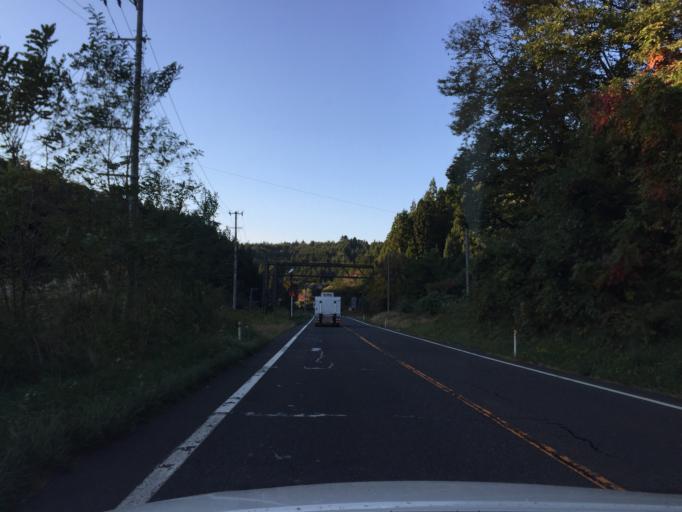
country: JP
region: Fukushima
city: Ishikawa
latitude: 37.2096
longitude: 140.6081
